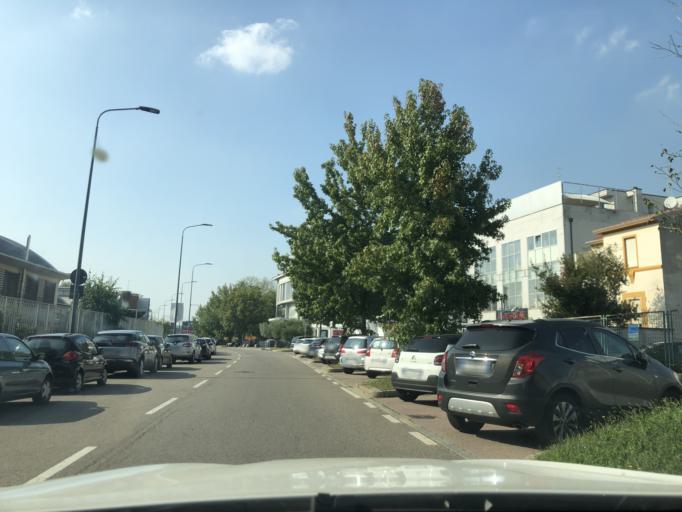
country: IT
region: Lombardy
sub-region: Citta metropolitana di Milano
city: Baranzate
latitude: 45.5006
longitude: 9.1230
